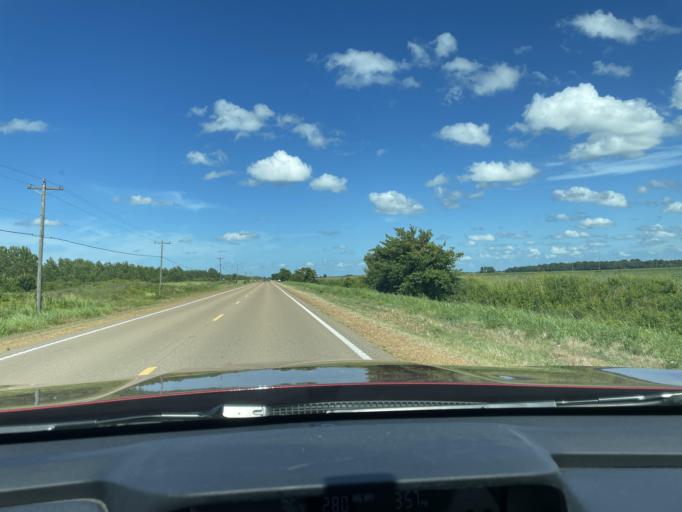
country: US
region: Mississippi
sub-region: Humphreys County
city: Belzoni
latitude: 33.1830
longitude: -90.6126
